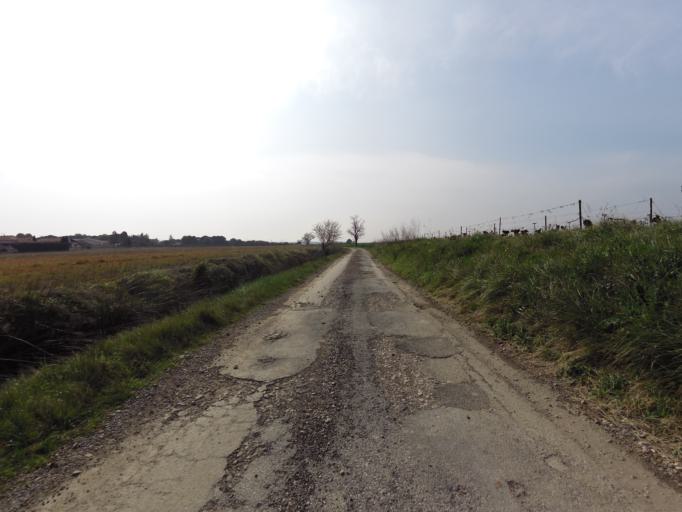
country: FR
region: Languedoc-Roussillon
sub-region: Departement du Gard
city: Calvisson
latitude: 43.7779
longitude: 4.2065
